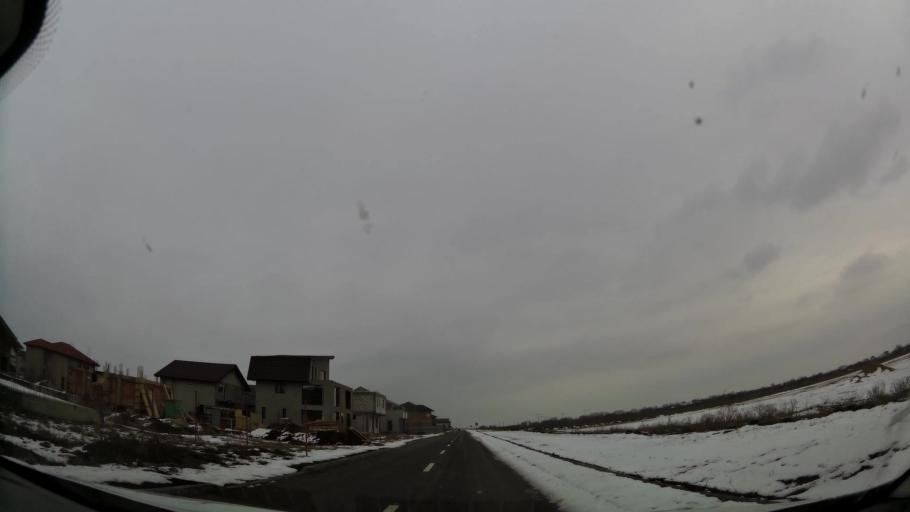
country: RO
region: Ilfov
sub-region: Comuna Tunari
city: Tunari
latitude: 44.5519
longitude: 26.1534
